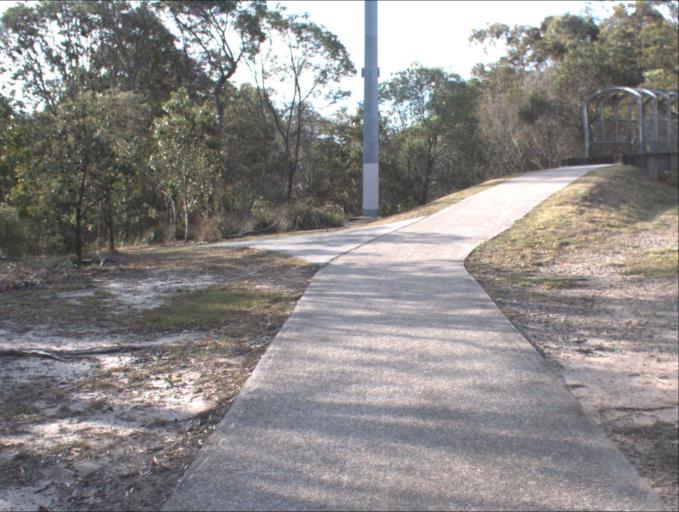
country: AU
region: Queensland
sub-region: Logan
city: Slacks Creek
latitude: -27.6282
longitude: 153.1460
